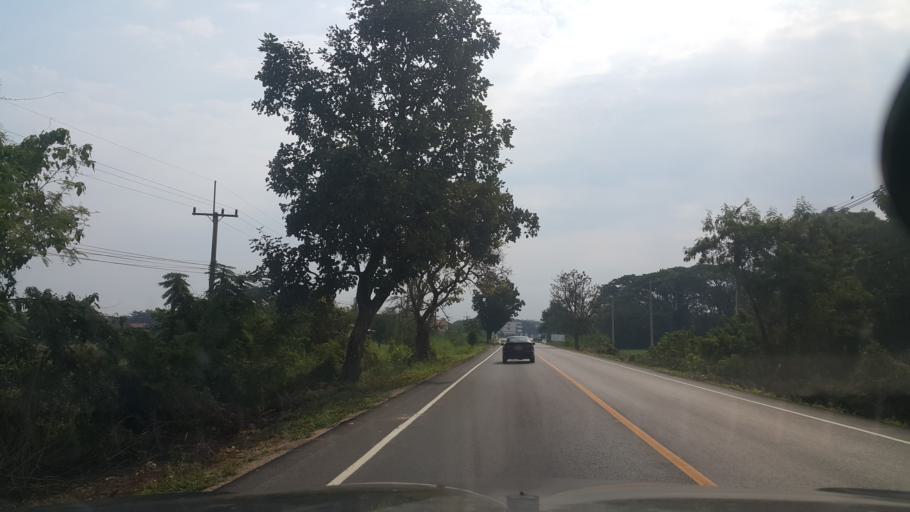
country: TH
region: Sukhothai
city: Si Samrong
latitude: 17.1772
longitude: 99.8473
